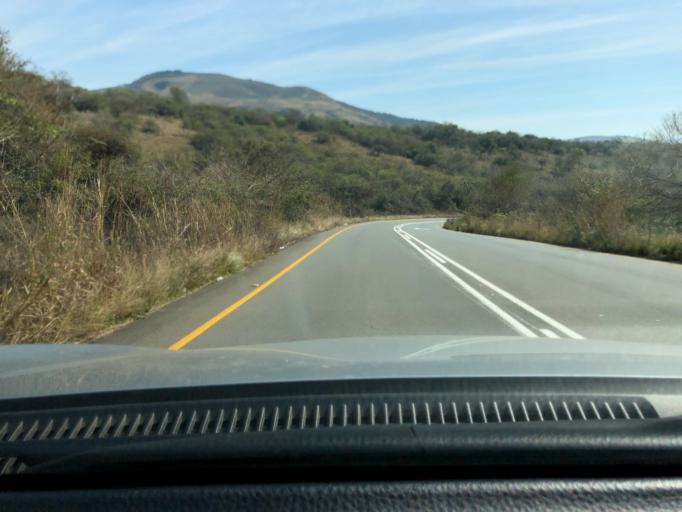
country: ZA
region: KwaZulu-Natal
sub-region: uMgungundlovu District Municipality
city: Richmond
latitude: -29.9822
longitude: 30.2485
